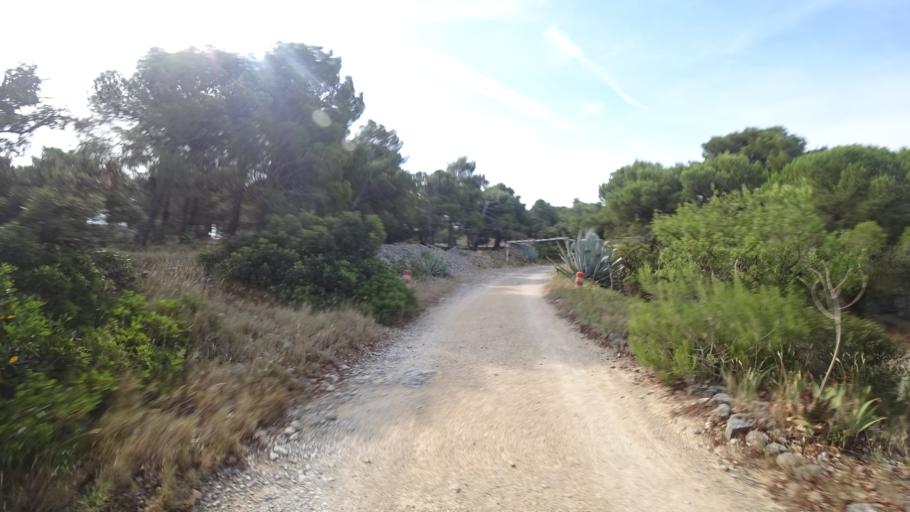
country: FR
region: Languedoc-Roussillon
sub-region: Departement de l'Aude
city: Leucate
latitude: 42.9011
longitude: 3.0323
